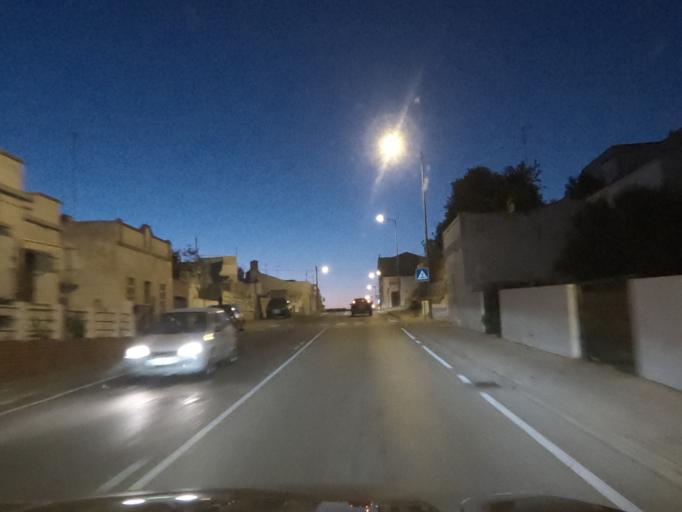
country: PT
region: Faro
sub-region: Loule
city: Loule
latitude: 37.1224
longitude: -8.0146
